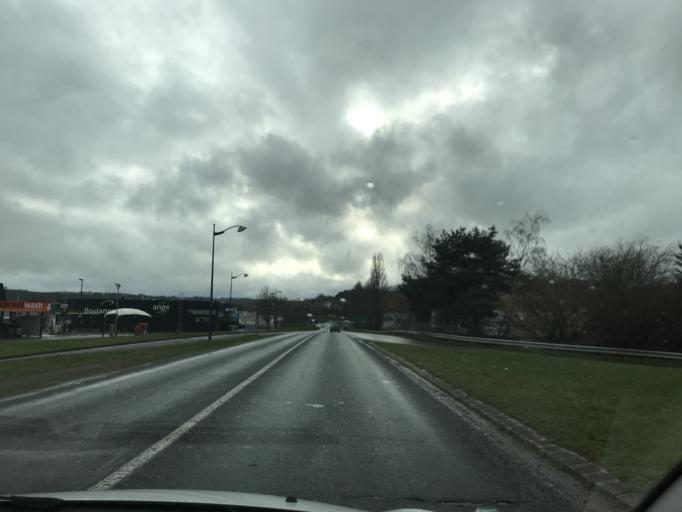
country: FR
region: Picardie
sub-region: Departement de l'Aisne
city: Soissons
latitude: 49.3686
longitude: 3.3160
